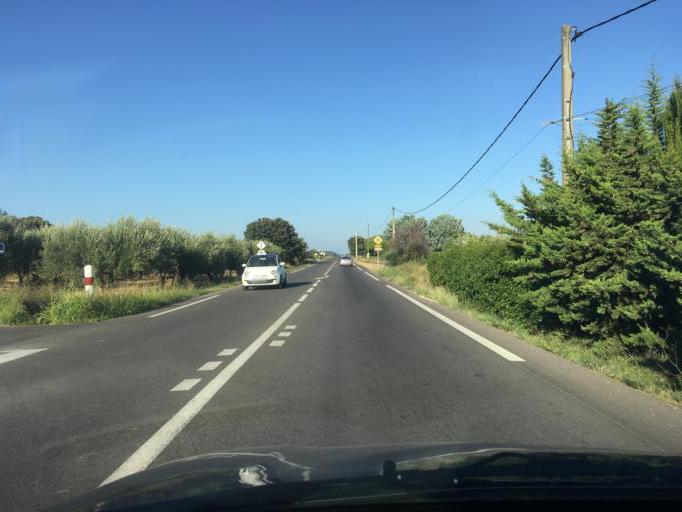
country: FR
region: Languedoc-Roussillon
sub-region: Departement du Gard
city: Bezouce
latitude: 43.8861
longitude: 4.4983
